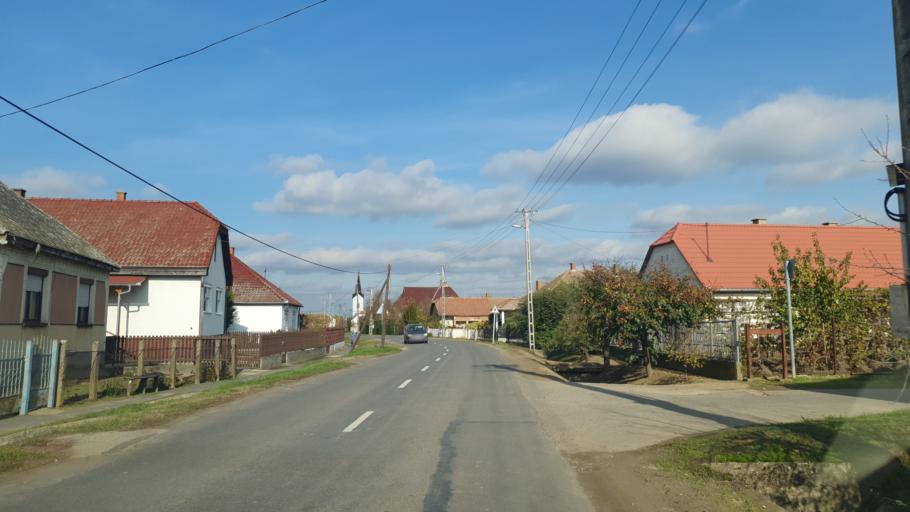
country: HU
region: Szabolcs-Szatmar-Bereg
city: Petnehaza
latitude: 48.0537
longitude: 22.0434
